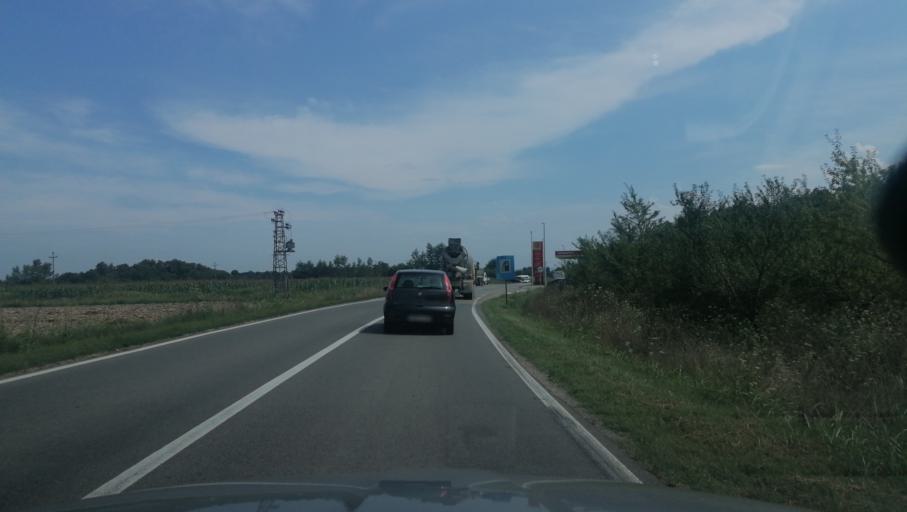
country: BA
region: Republika Srpska
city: Velika Obarska
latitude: 44.7741
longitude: 19.1165
